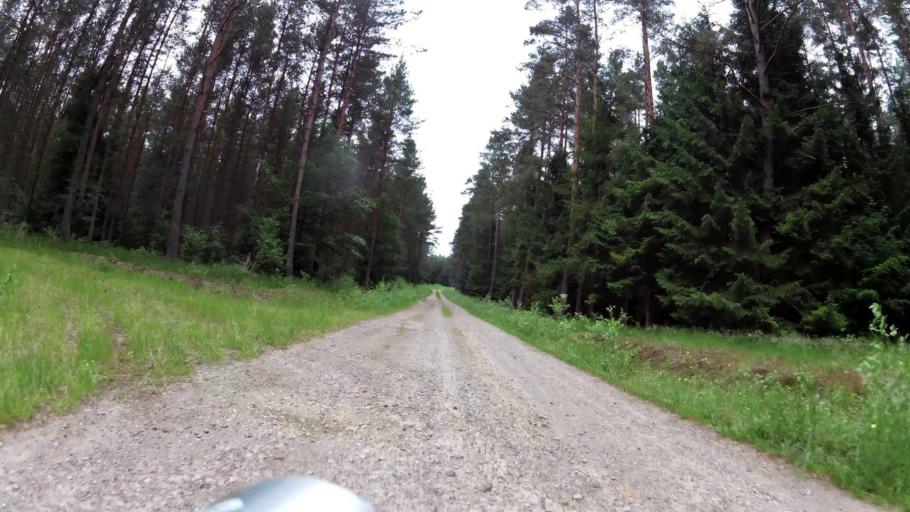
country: PL
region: West Pomeranian Voivodeship
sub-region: Powiat szczecinecki
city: Bialy Bor
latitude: 53.9161
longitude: 16.8307
